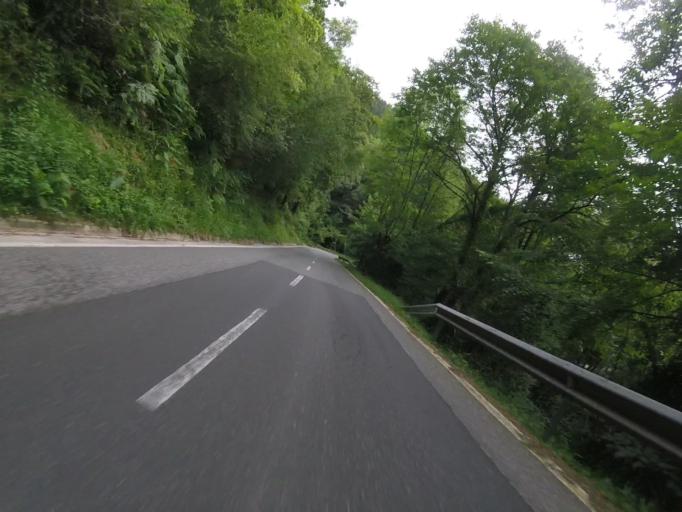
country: ES
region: Navarre
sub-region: Provincia de Navarra
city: Zubieta
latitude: 43.1229
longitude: -1.7530
